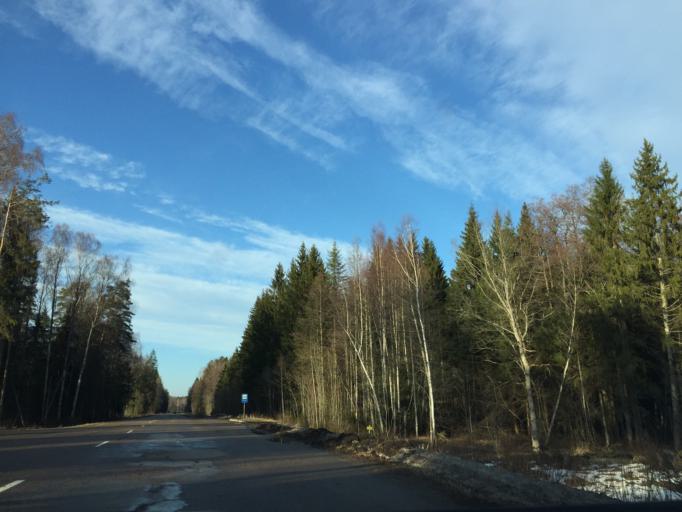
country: LV
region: Kekava
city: Balozi
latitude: 56.7411
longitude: 24.1085
